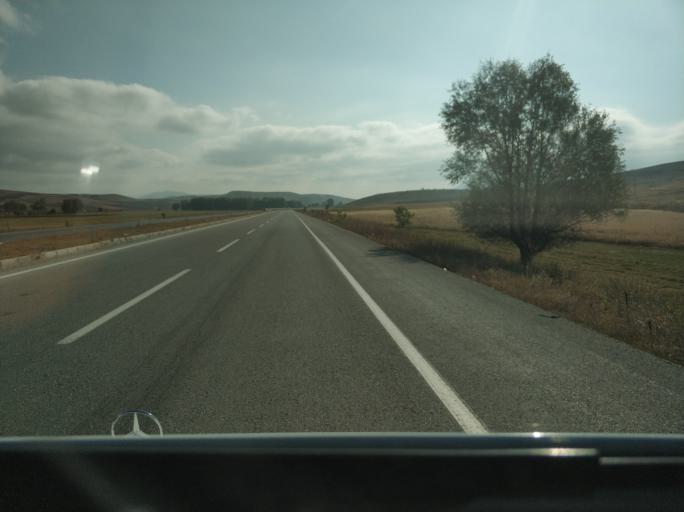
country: TR
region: Sivas
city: Yildizeli
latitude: 39.8490
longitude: 36.4931
